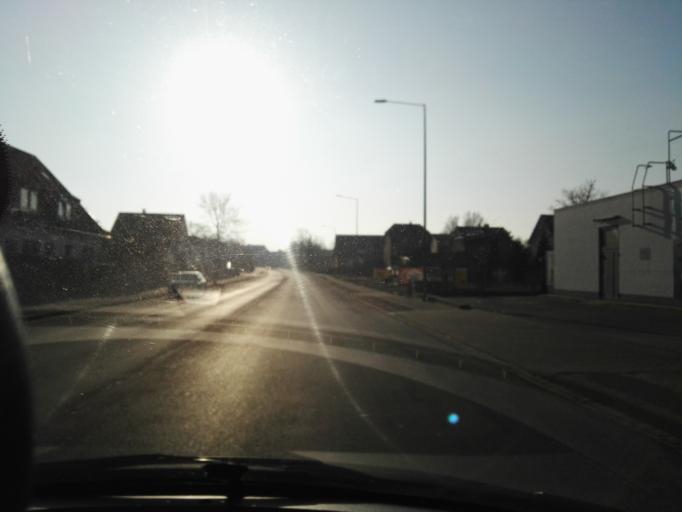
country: DE
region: Lower Saxony
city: Sarstedt
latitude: 52.2354
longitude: 9.8464
